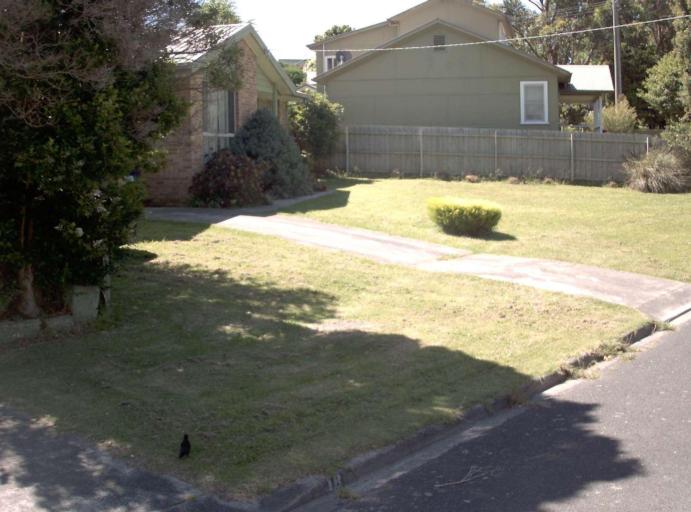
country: AU
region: Victoria
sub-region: Latrobe
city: Morwell
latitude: -38.6535
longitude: 146.1952
